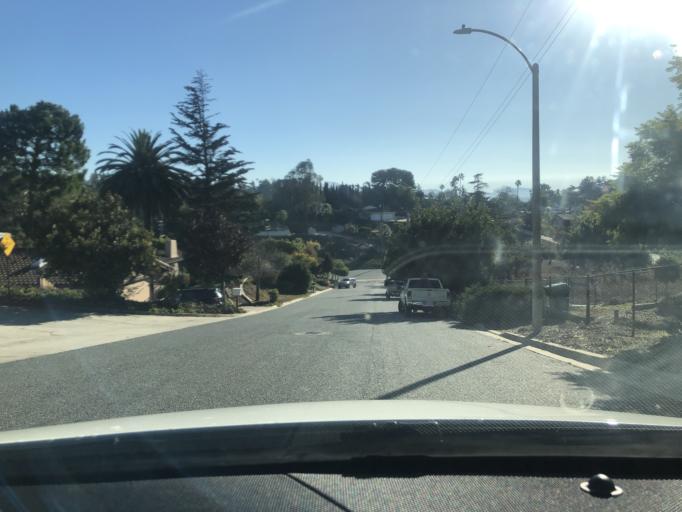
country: US
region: California
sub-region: San Diego County
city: Casa de Oro-Mount Helix
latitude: 32.7681
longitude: -116.9603
